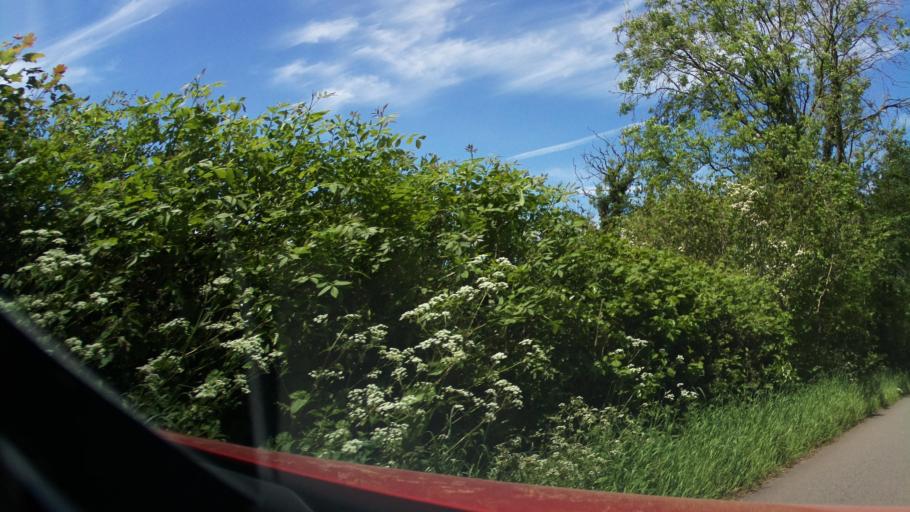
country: GB
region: Wales
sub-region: Monmouthshire
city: Llangwm
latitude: 51.7189
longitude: -2.7635
